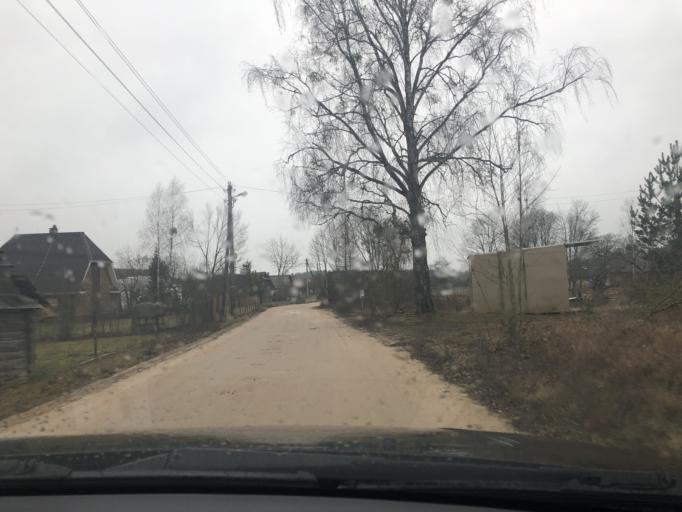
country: BY
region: Grodnenskaya
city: Skidal'
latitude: 53.8596
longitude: 24.2479
